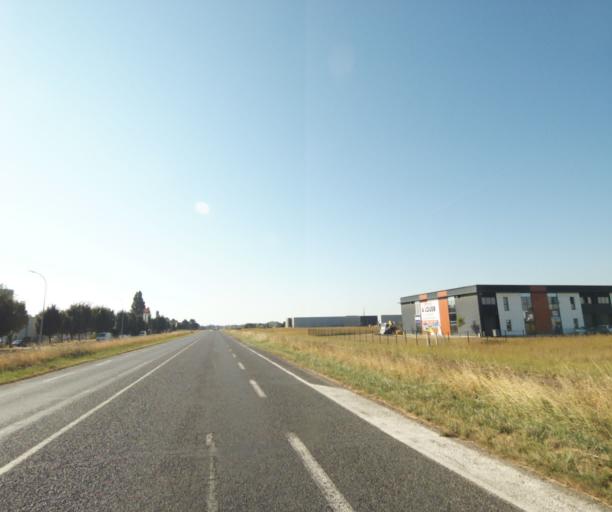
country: FR
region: Ile-de-France
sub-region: Departement de Seine-et-Marne
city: Lieusaint
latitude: 48.6204
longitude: 2.5648
